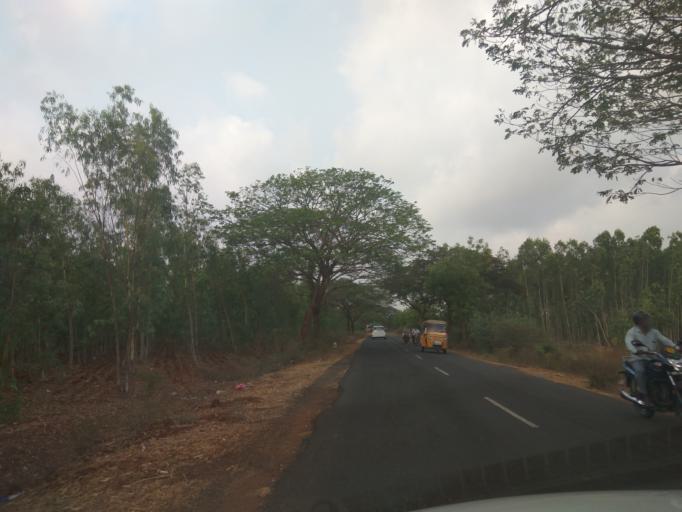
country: IN
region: Andhra Pradesh
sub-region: Prakasam
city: Kandukur
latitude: 15.1976
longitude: 79.8433
